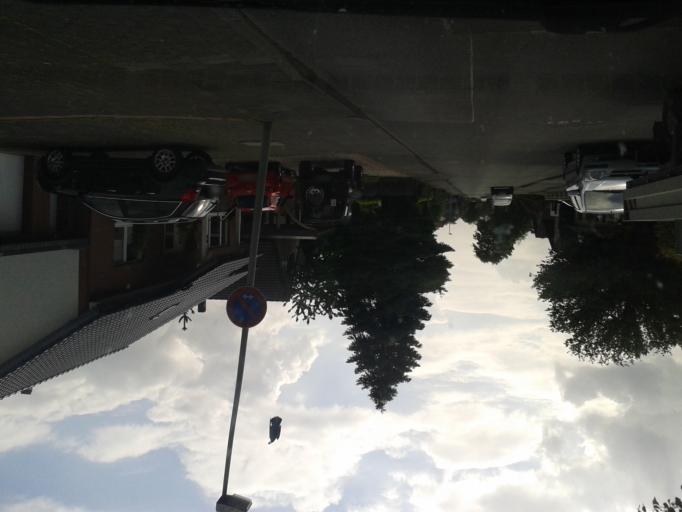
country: DE
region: North Rhine-Westphalia
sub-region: Regierungsbezirk Detmold
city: Paderborn
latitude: 51.7447
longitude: 8.6897
